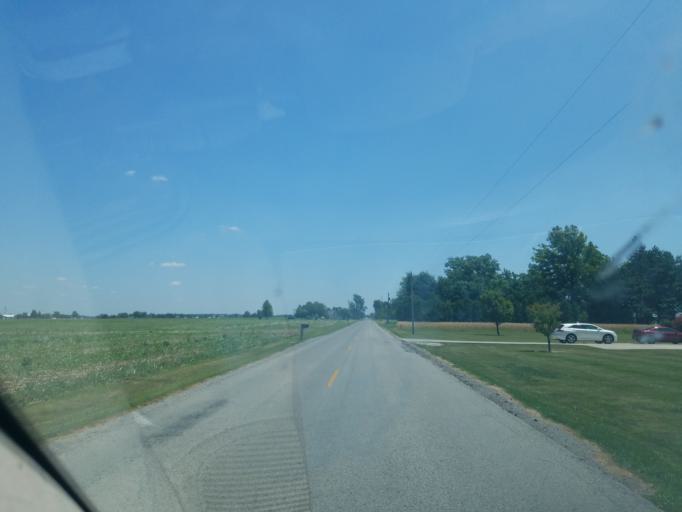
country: US
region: Ohio
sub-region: Allen County
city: Elida
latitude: 40.7871
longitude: -84.2732
